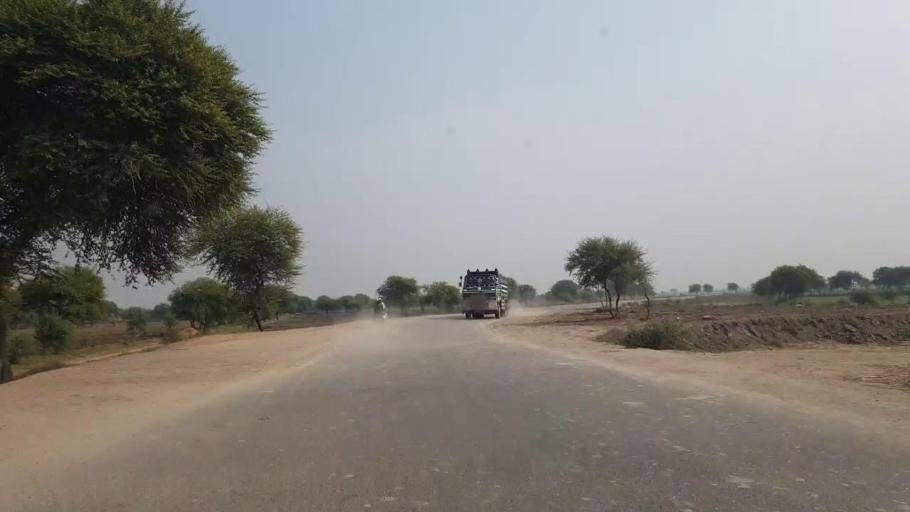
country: PK
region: Sindh
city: Matli
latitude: 25.0619
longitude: 68.6651
